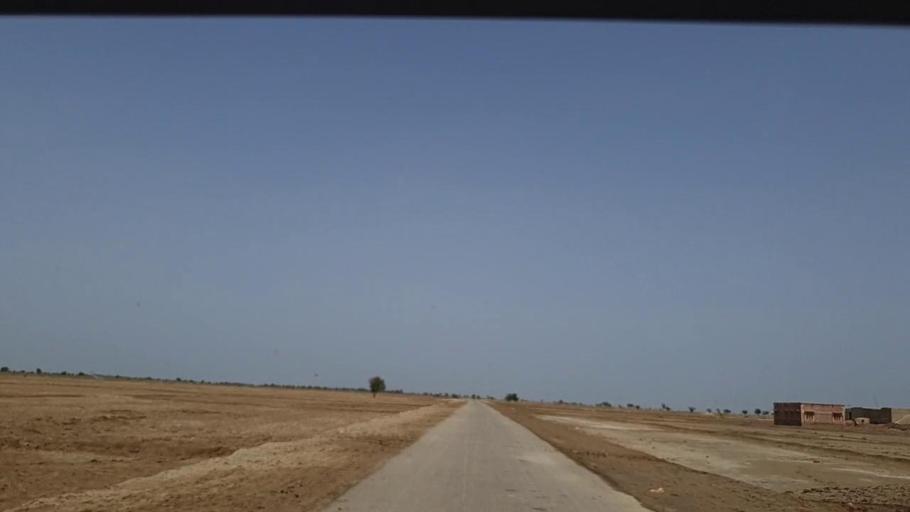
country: PK
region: Sindh
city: Johi
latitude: 26.7707
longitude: 67.6462
